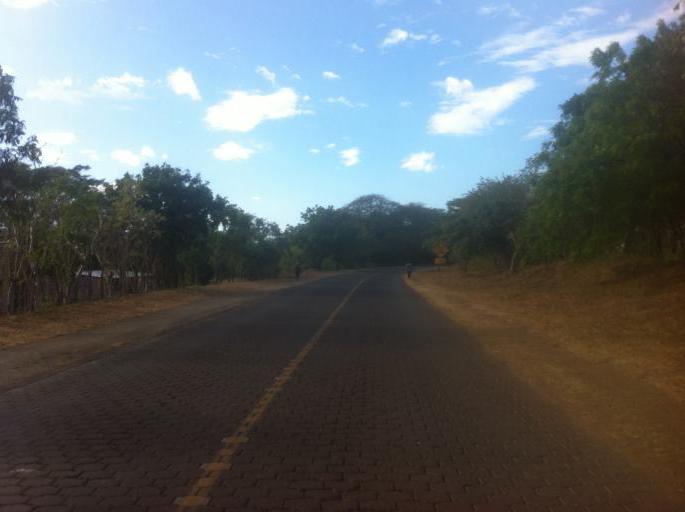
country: NI
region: Managua
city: Masachapa
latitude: 11.8310
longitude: -86.5069
